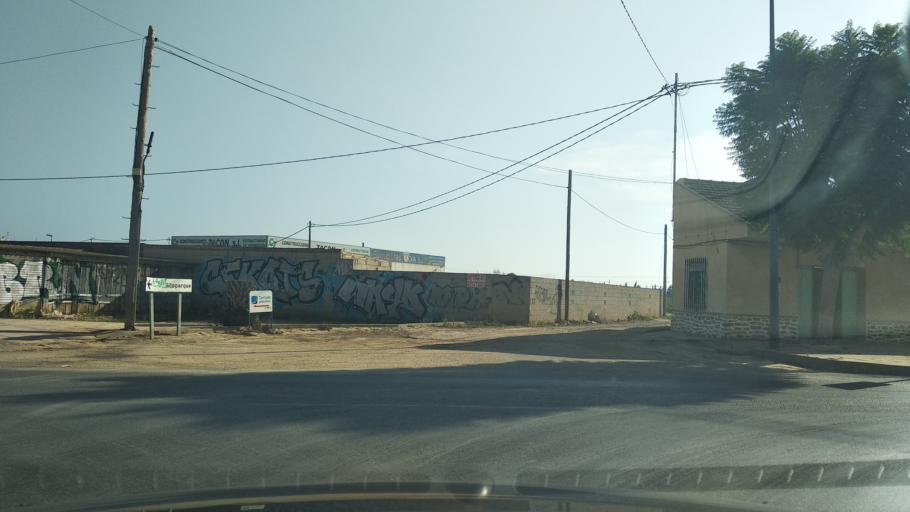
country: ES
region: Murcia
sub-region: Murcia
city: San Javier
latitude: 37.8062
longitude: -0.8445
